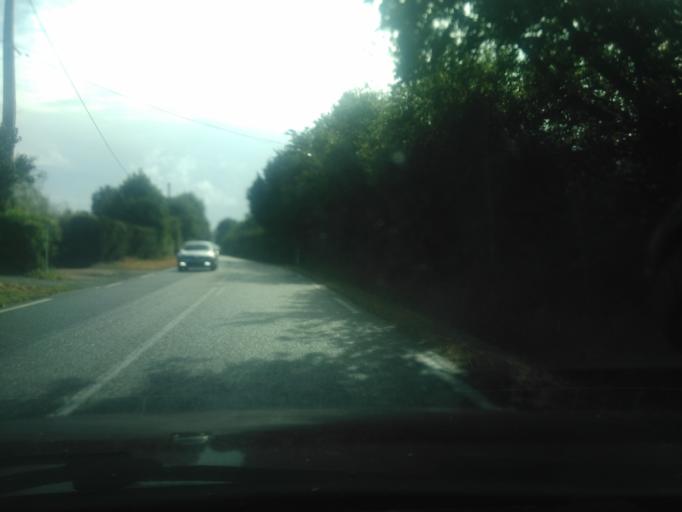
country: FR
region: Poitou-Charentes
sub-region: Departement des Deux-Sevres
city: Le Tallud
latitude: 46.6270
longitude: -0.3125
